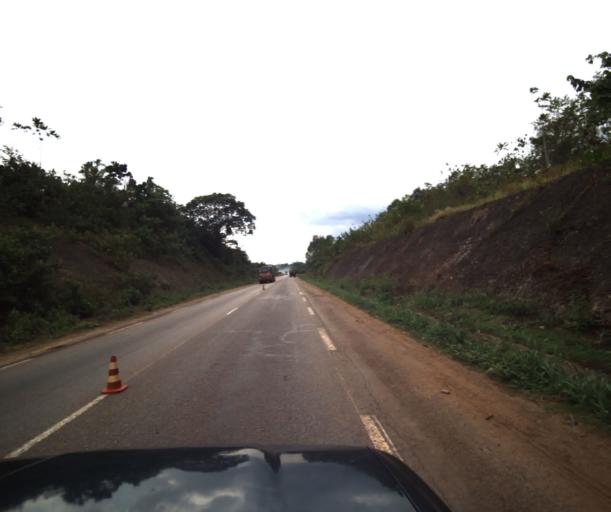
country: CM
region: Littoral
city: Edea
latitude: 3.9483
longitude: 10.0377
